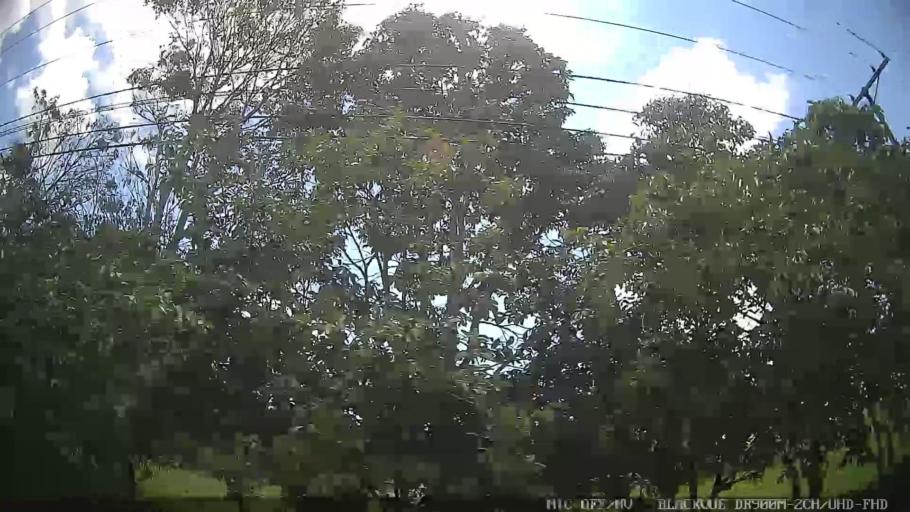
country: BR
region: Sao Paulo
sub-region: Itatiba
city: Itatiba
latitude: -22.8712
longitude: -46.7893
